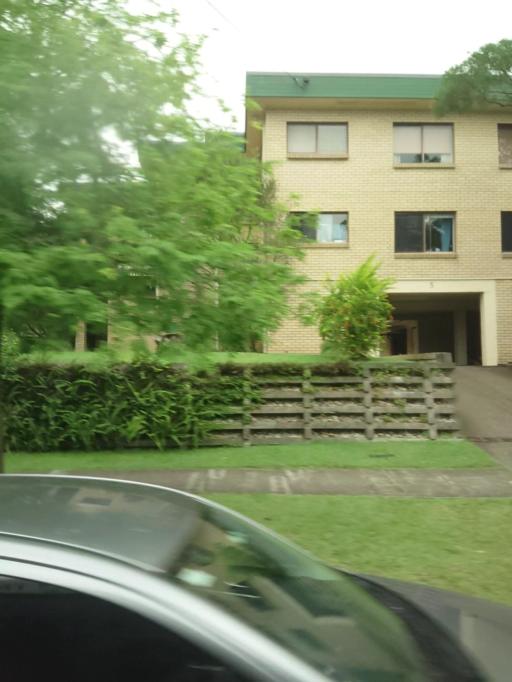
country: AU
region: Queensland
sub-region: Brisbane
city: Morningside
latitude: -27.4714
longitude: 153.0728
